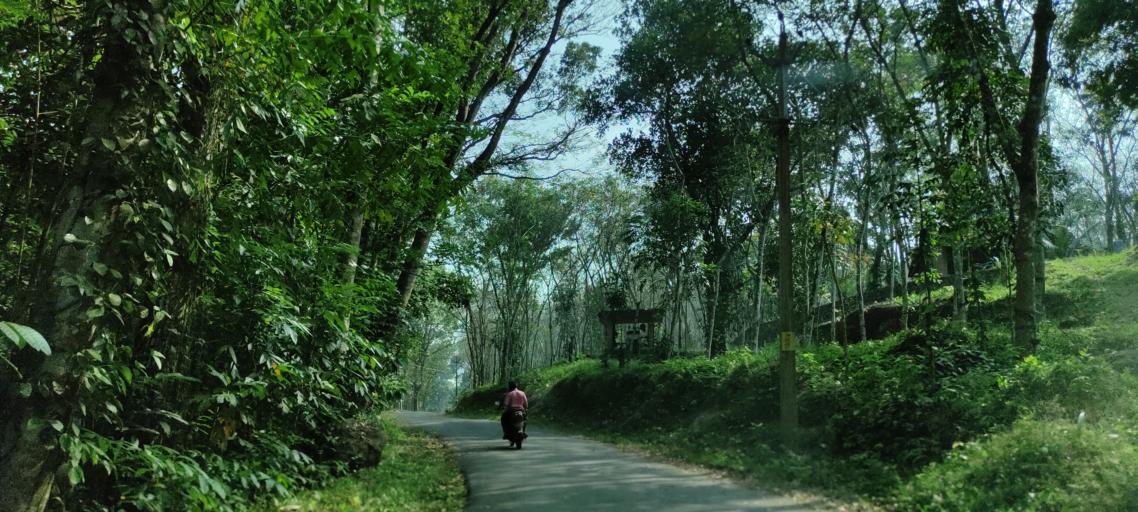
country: IN
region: Kerala
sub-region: Ernakulam
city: Piravam
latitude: 9.8092
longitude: 76.5251
